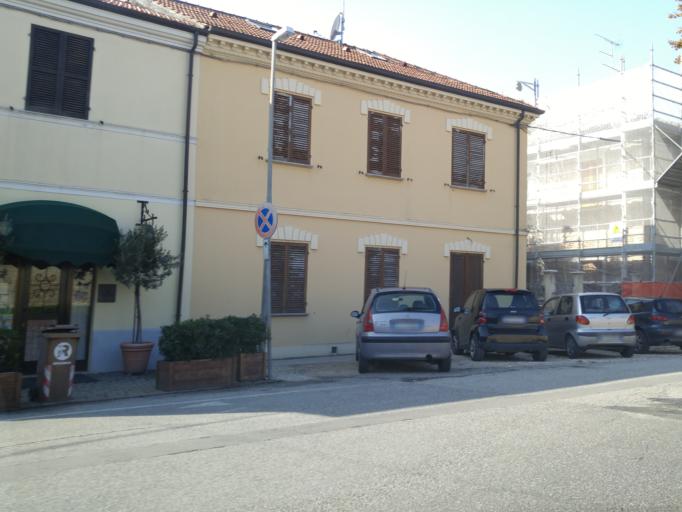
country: IT
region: The Marches
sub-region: Provincia di Pesaro e Urbino
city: Fano
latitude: 43.8376
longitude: 13.0192
